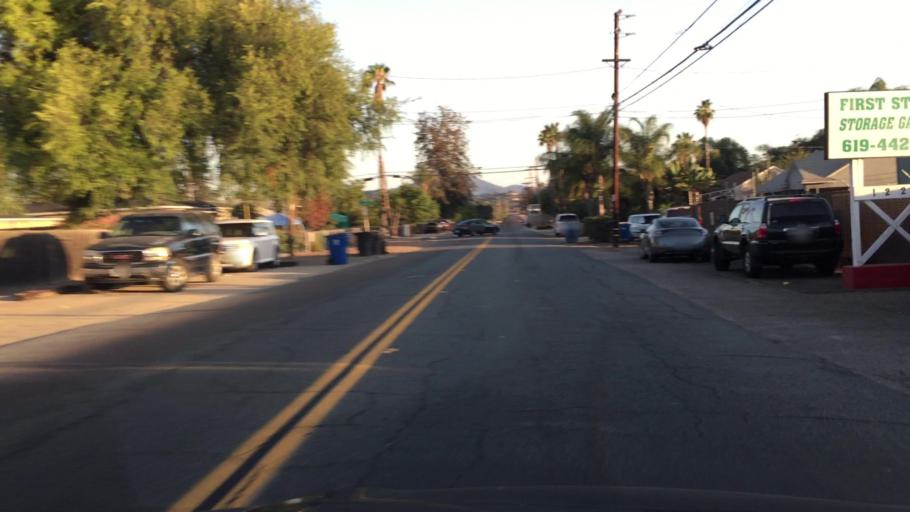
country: US
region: California
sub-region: San Diego County
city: Bostonia
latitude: 32.8122
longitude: -116.9446
